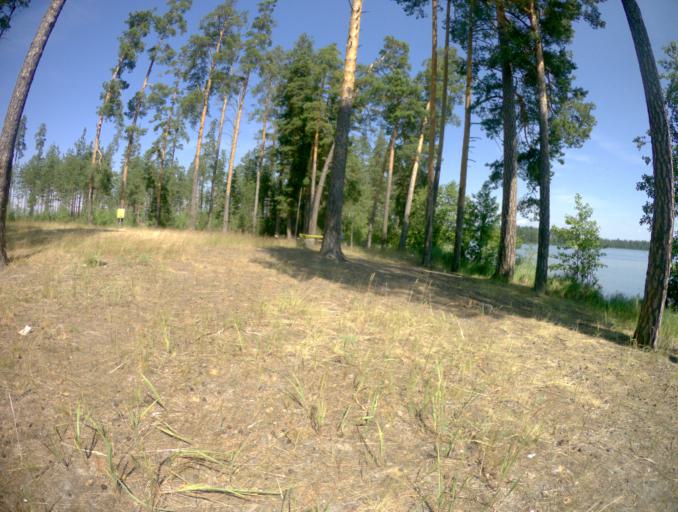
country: RU
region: Ivanovo
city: Talitsy
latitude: 56.4141
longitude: 42.2772
